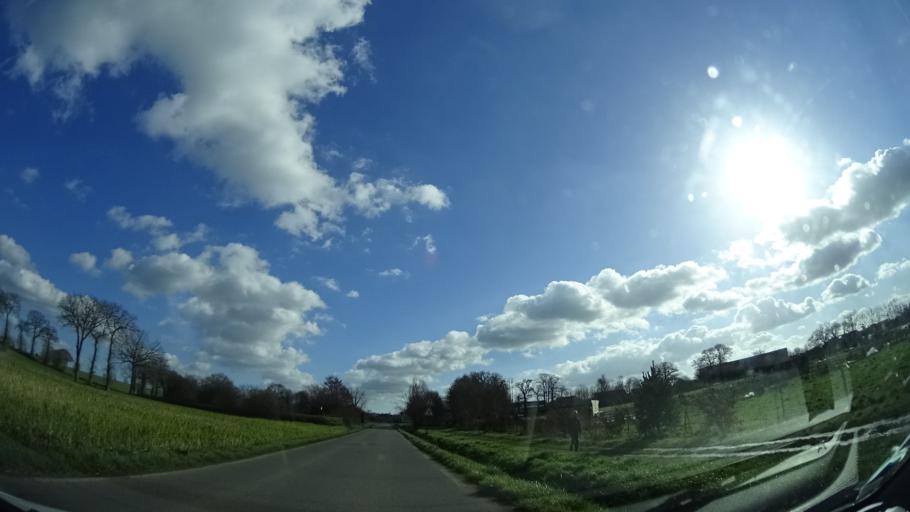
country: FR
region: Brittany
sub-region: Departement d'Ille-et-Vilaine
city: Pace
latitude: 48.1589
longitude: -1.7604
